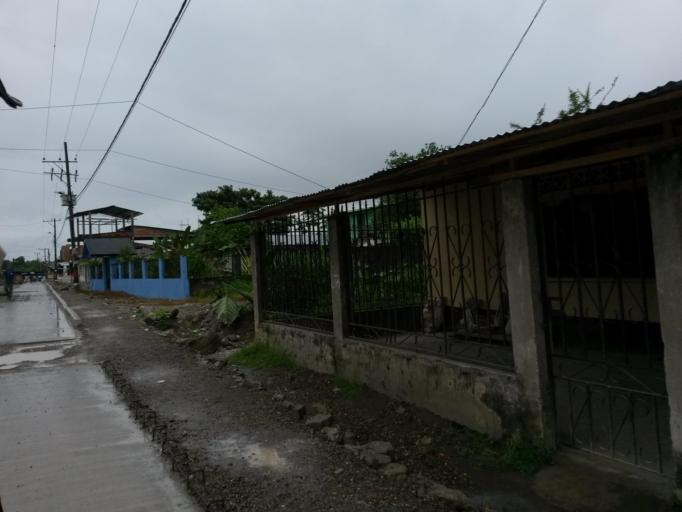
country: CO
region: Cauca
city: Guapi
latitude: 2.5733
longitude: -77.8931
